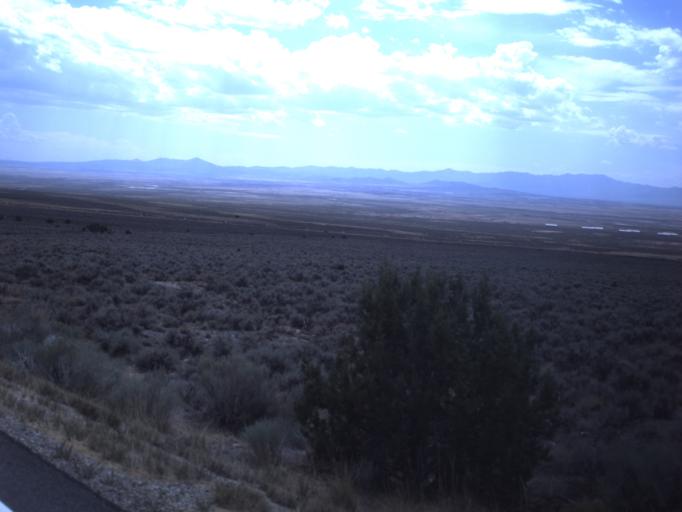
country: US
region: Utah
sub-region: Tooele County
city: Tooele
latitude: 40.3115
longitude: -112.2819
